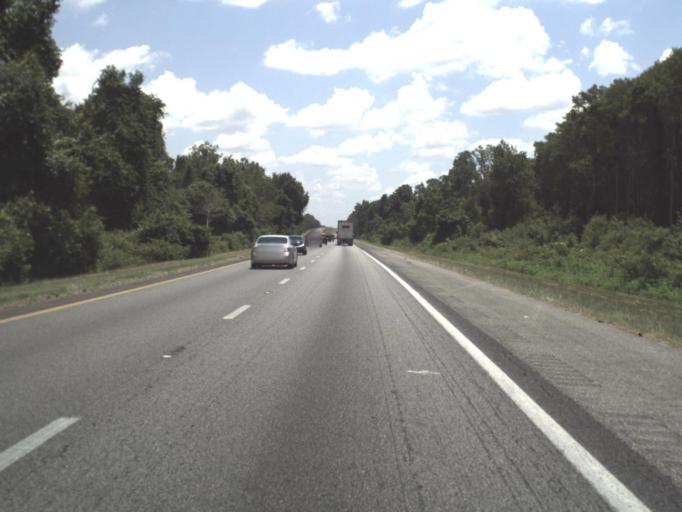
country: US
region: Florida
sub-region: Madison County
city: Madison
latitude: 30.4304
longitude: -83.5570
